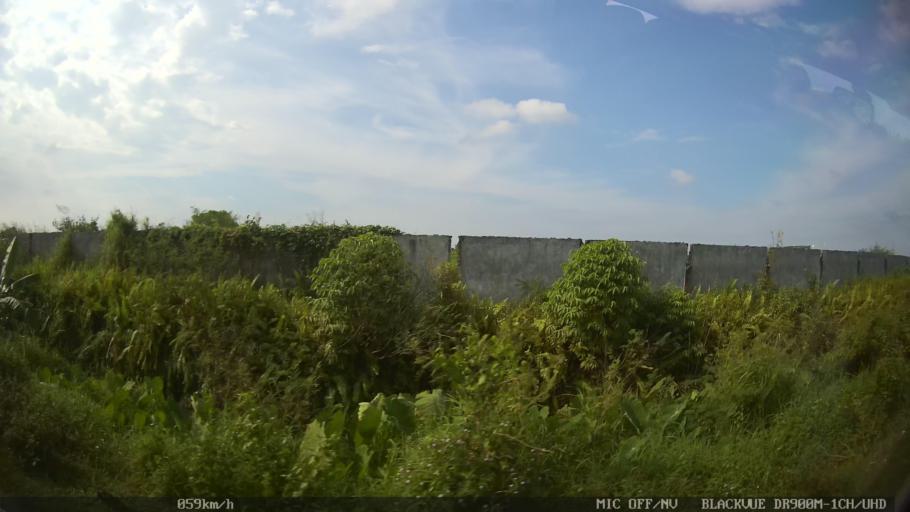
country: ID
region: North Sumatra
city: Medan
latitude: 3.5731
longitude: 98.7683
